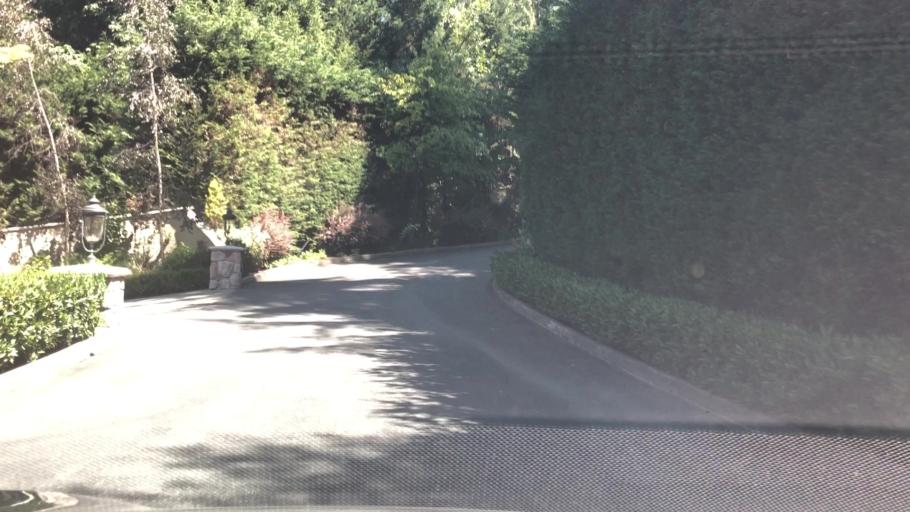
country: US
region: Washington
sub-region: King County
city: Cottage Lake
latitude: 47.7303
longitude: -122.0922
